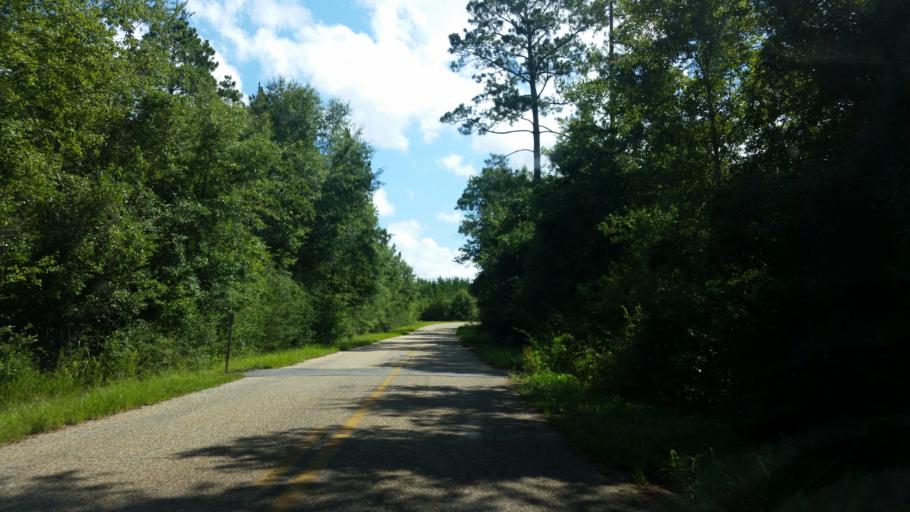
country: US
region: Florida
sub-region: Santa Rosa County
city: Point Baker
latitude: 30.7165
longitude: -86.9208
